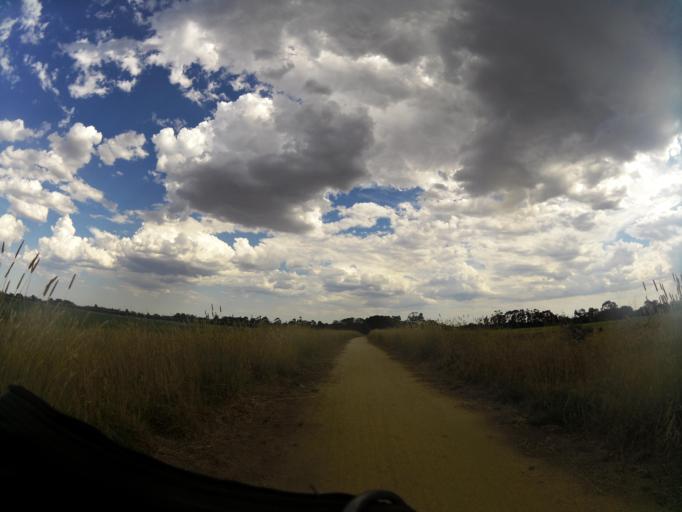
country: AU
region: Victoria
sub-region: Wellington
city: Heyfield
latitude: -38.0042
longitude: 146.6977
